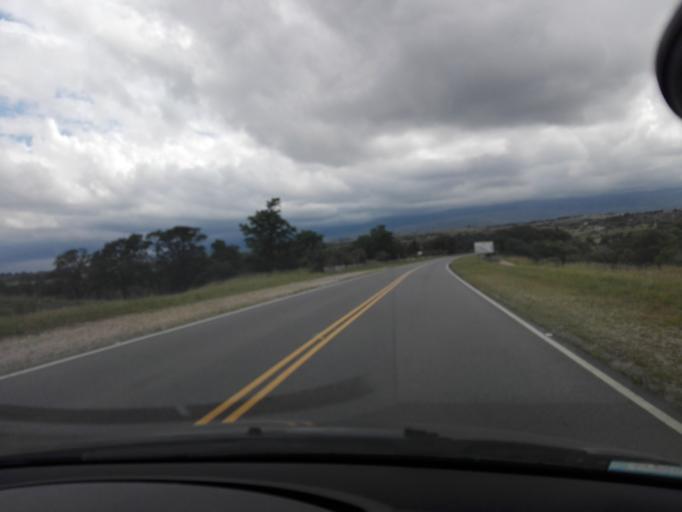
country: AR
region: Cordoba
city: Cuesta Blanca
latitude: -31.5737
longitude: -64.5914
